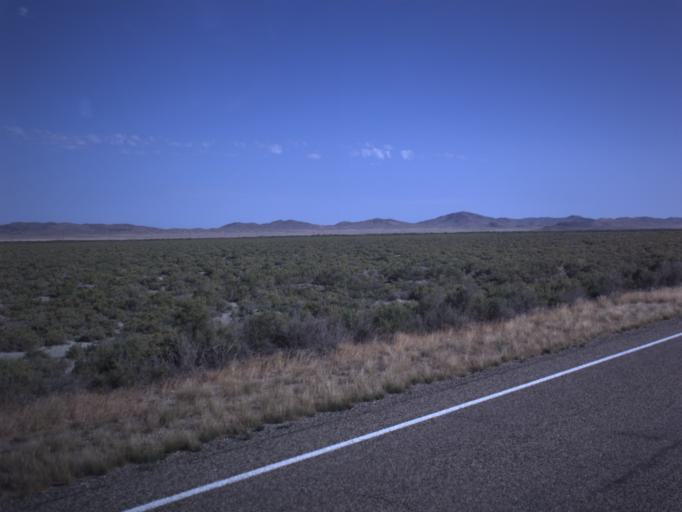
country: US
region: Utah
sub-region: Beaver County
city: Milford
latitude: 38.5995
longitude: -112.9874
